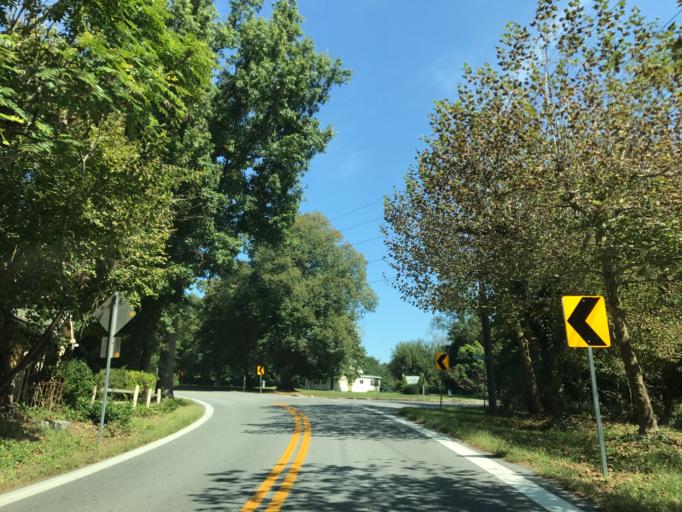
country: US
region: Delaware
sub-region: New Castle County
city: Townsend
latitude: 39.3728
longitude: -75.8028
